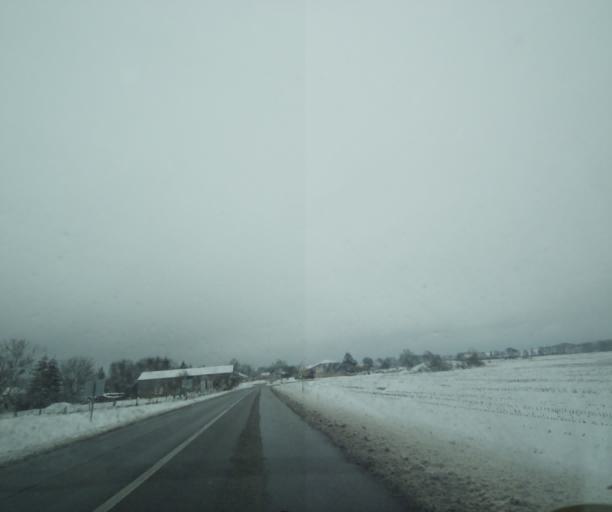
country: FR
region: Champagne-Ardenne
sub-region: Departement de la Haute-Marne
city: Montier-en-Der
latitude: 48.5038
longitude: 4.7893
